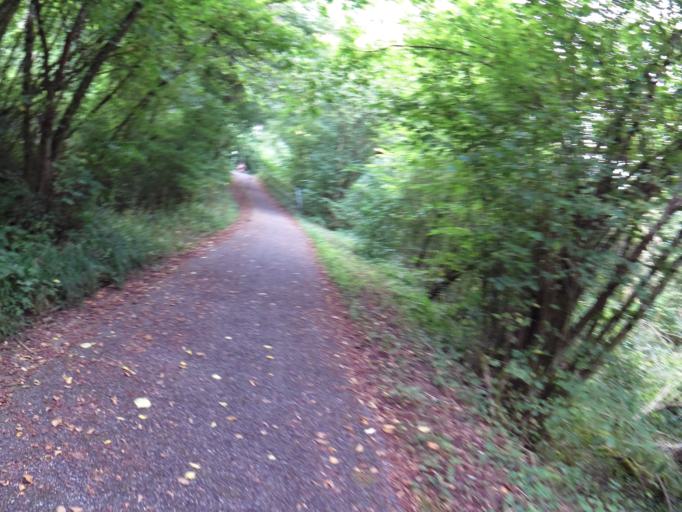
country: DE
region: Rheinland-Pfalz
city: Metterich
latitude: 49.9824
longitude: 6.5718
